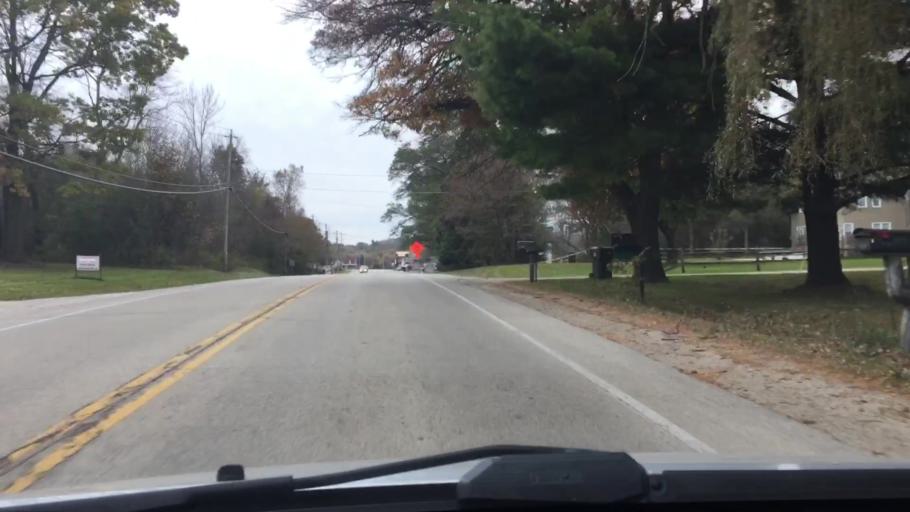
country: US
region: Wisconsin
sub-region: Waukesha County
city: New Berlin
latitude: 42.9542
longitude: -88.1432
